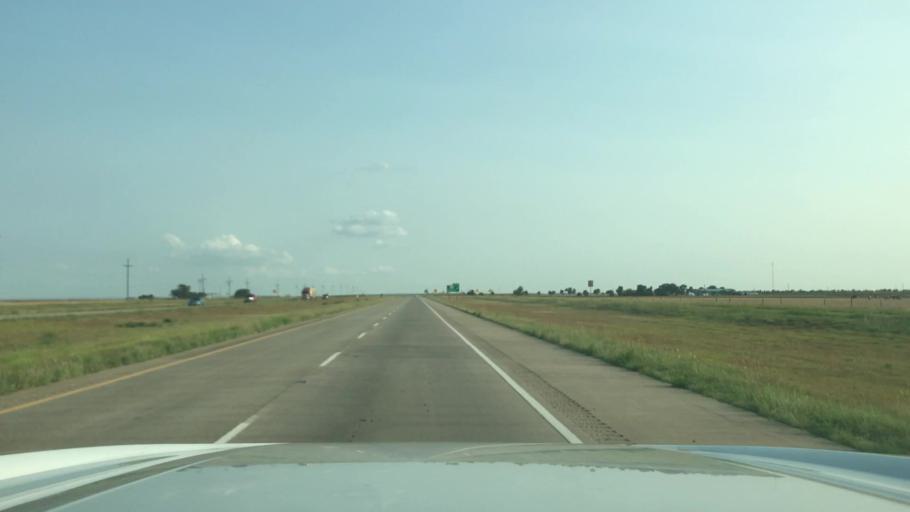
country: US
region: Texas
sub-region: Randall County
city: Canyon
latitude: 34.8185
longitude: -101.8488
